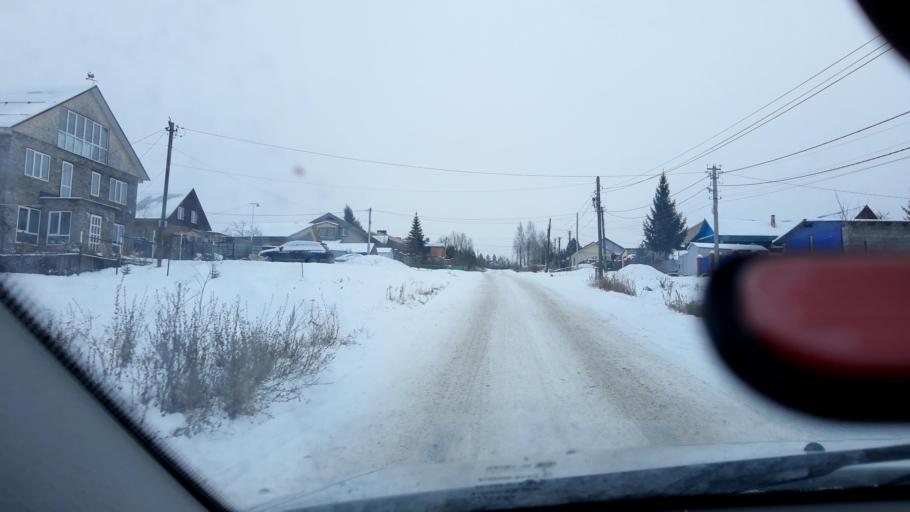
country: RU
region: Bashkortostan
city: Kabakovo
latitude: 54.6363
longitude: 56.0816
